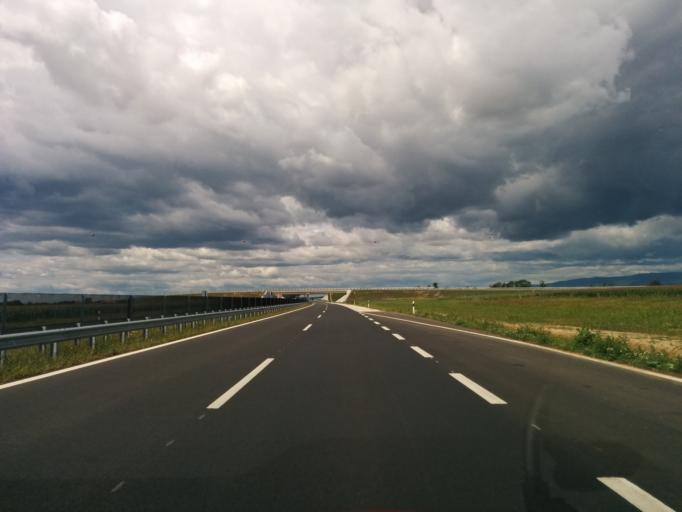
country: HU
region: Vas
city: Vep
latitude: 47.2553
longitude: 16.7015
